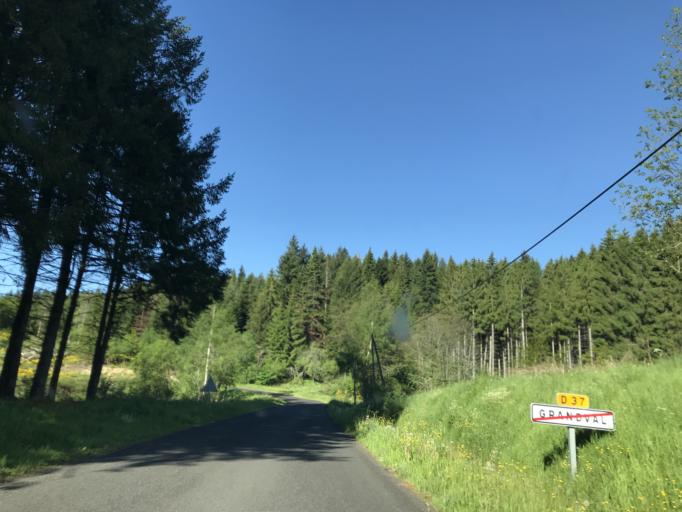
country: FR
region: Auvergne
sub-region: Departement du Puy-de-Dome
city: Cunlhat
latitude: 45.5966
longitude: 3.6436
